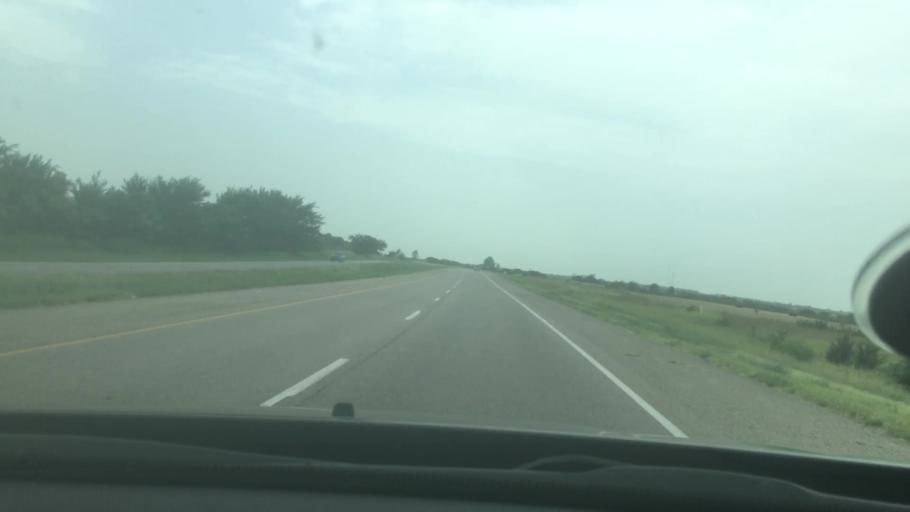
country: US
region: Oklahoma
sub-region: Pontotoc County
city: Ada
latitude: 34.7140
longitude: -96.7266
